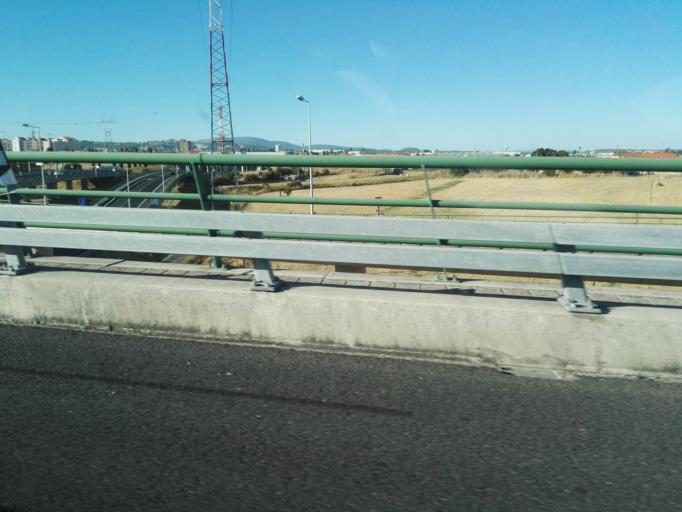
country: PT
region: Lisbon
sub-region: Alenquer
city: Carregado
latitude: 39.0174
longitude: -8.9638
